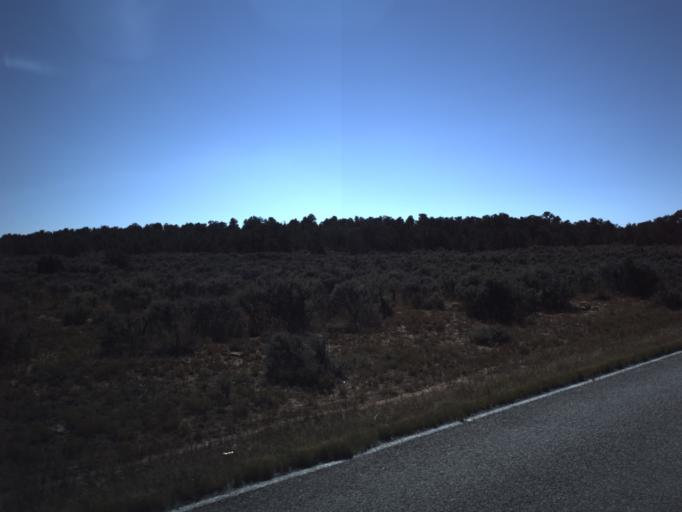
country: US
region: Utah
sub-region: San Juan County
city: Blanding
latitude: 37.4232
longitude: -109.9407
